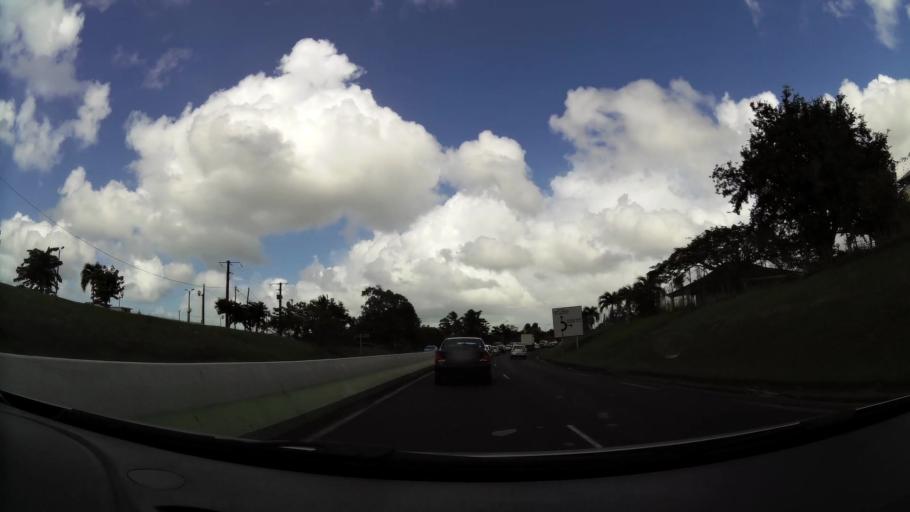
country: MQ
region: Martinique
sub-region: Martinique
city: Ducos
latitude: 14.5304
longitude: -60.9831
